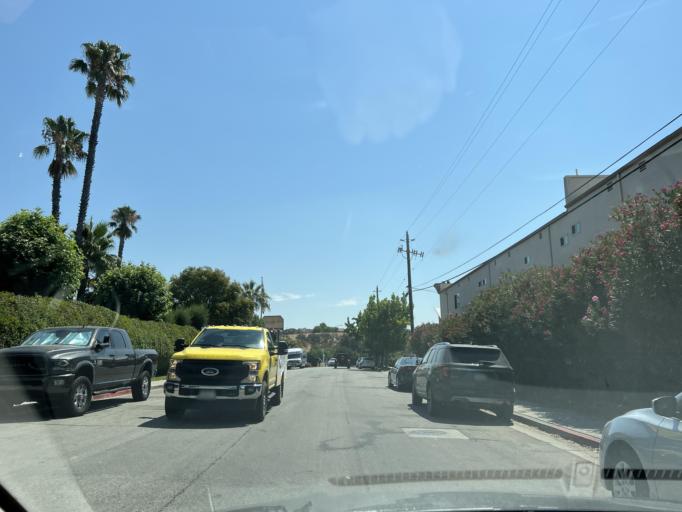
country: US
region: California
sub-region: San Luis Obispo County
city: Paso Robles
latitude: 35.6420
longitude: -120.6879
